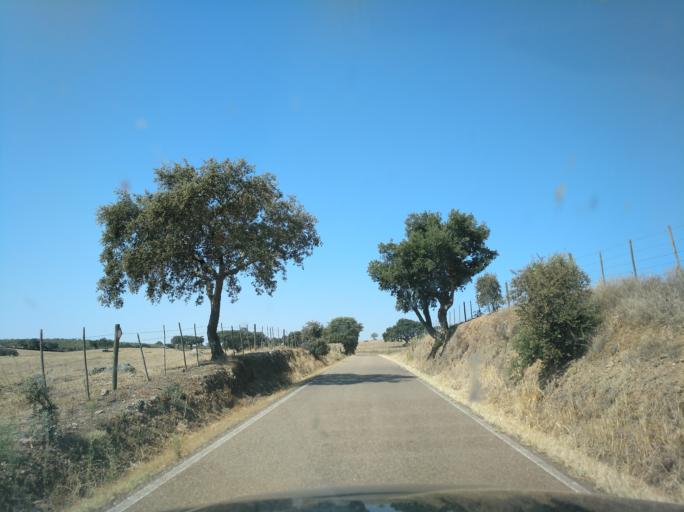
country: PT
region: Portalegre
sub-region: Campo Maior
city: Campo Maior
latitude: 39.0452
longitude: -7.0221
